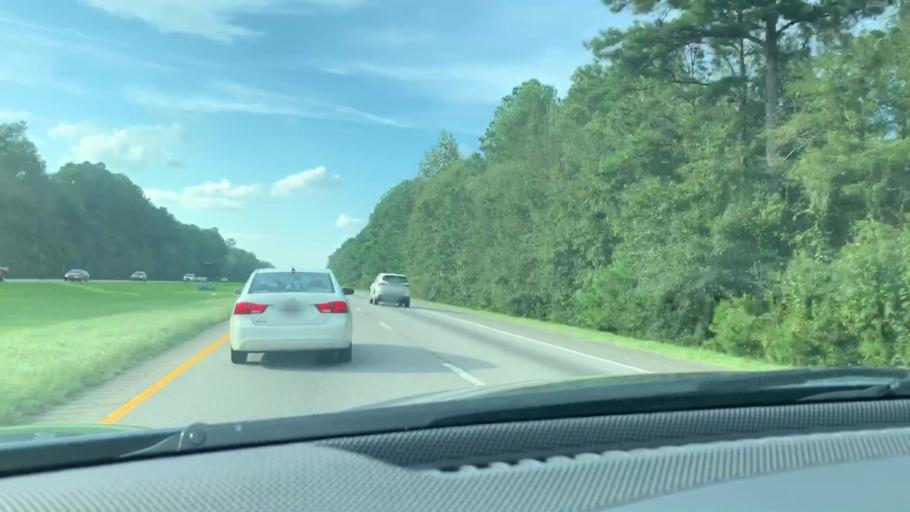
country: US
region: South Carolina
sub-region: Orangeburg County
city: Brookdale
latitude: 33.4404
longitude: -80.7062
